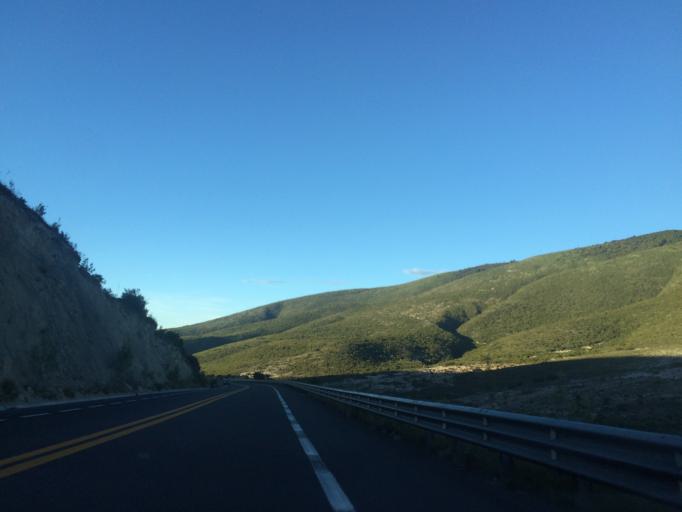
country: MX
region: Puebla
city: Morelos Canada
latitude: 18.6782
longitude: -97.4603
